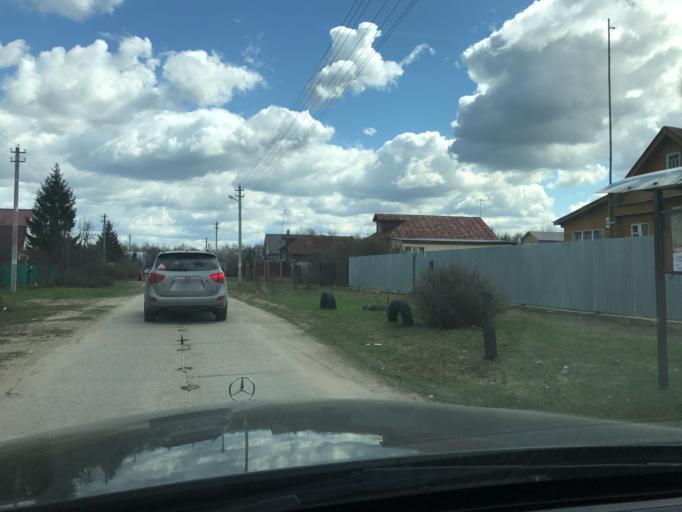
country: RU
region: Vladimir
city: Pokrov
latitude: 55.8538
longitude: 39.1964
